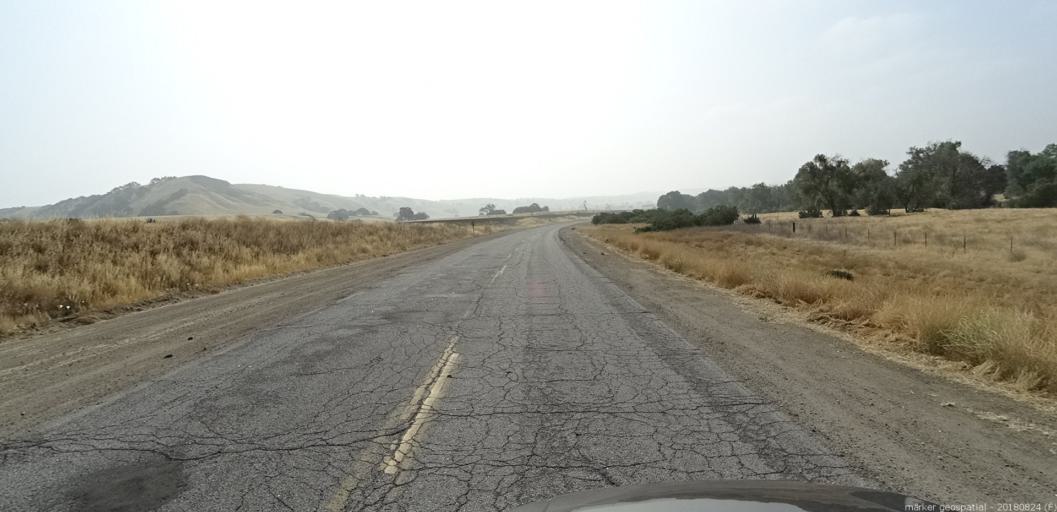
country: US
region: California
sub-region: San Luis Obispo County
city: San Miguel
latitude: 35.8615
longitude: -120.7695
